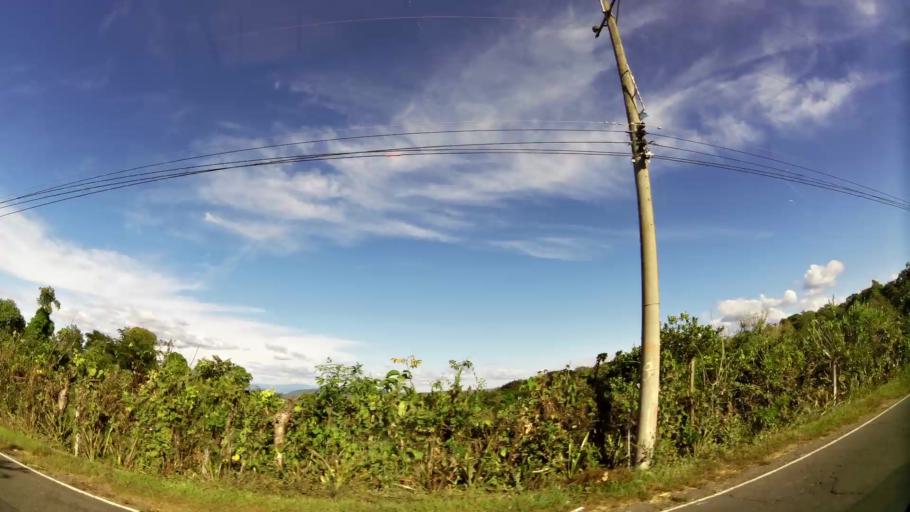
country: SV
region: Cuscatlan
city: Tenancingo
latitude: 13.8479
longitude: -89.0332
